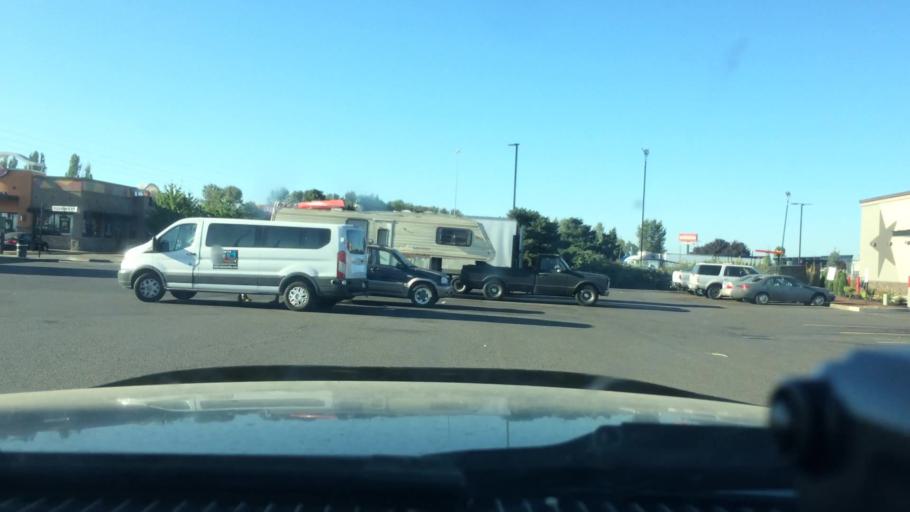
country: US
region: Oregon
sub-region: Marion County
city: Hayesville
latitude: 45.0494
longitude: -122.9757
